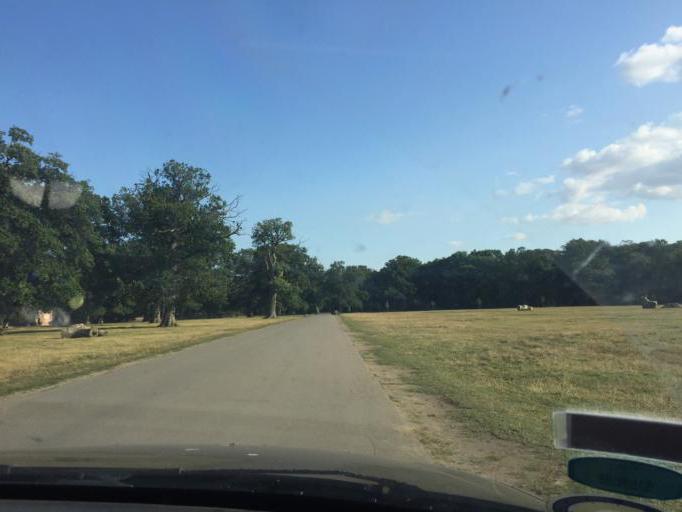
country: DK
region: Zealand
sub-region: Lolland Kommune
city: Maribo
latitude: 54.8164
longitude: 11.5100
